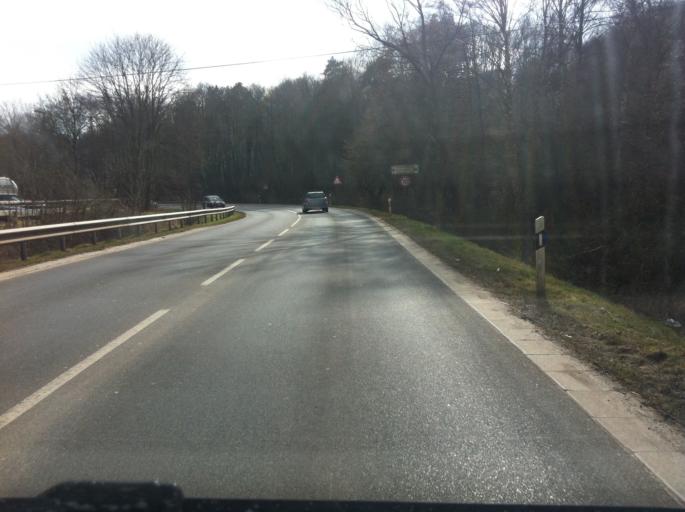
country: DE
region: North Rhine-Westphalia
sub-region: Regierungsbezirk Koln
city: Mechernich
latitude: 50.5979
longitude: 6.6314
